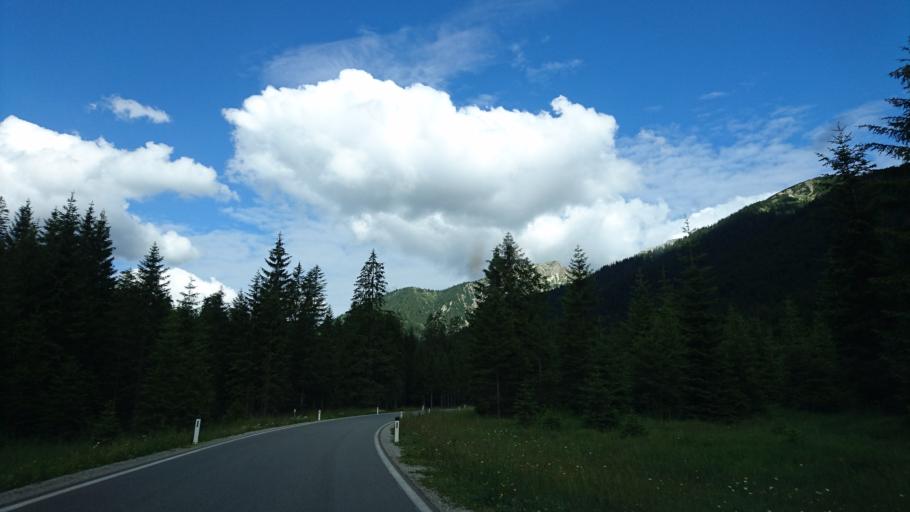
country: DE
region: Bavaria
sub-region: Swabia
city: Halblech
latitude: 47.5331
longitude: 10.8830
